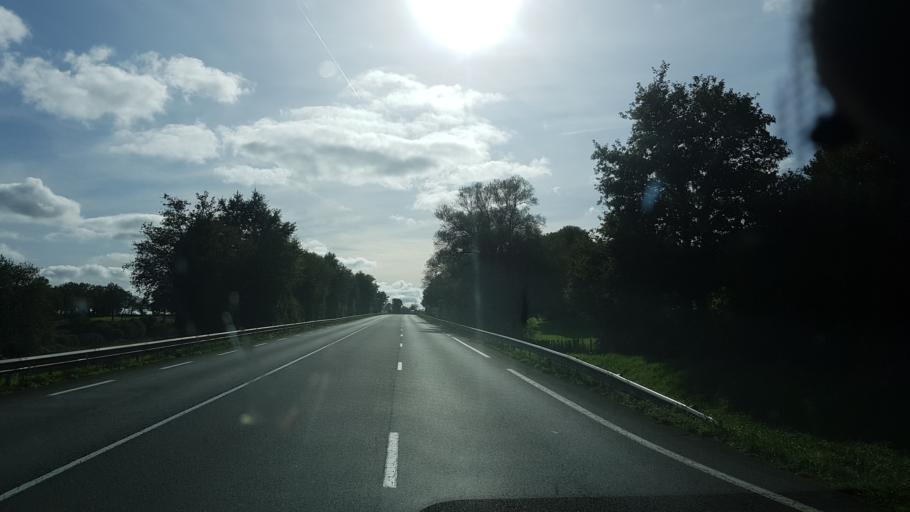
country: FR
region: Poitou-Charentes
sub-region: Departement de la Charente
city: Confolens
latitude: 46.0117
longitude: 0.6437
